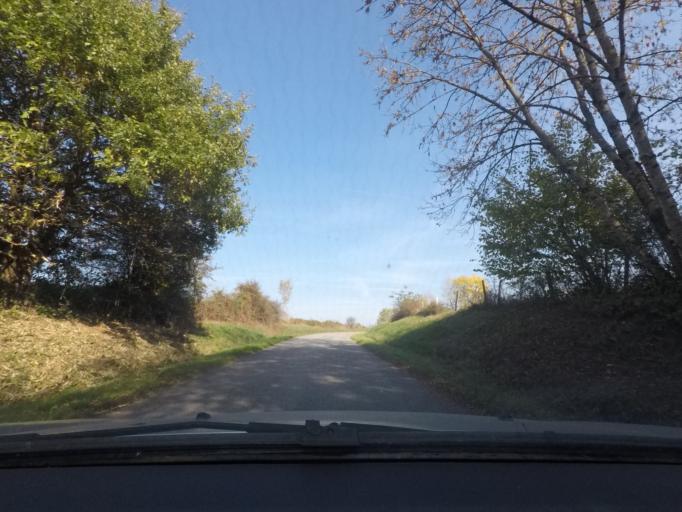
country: BE
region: Wallonia
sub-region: Province du Luxembourg
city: Tintigny
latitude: 49.6994
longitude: 5.4981
